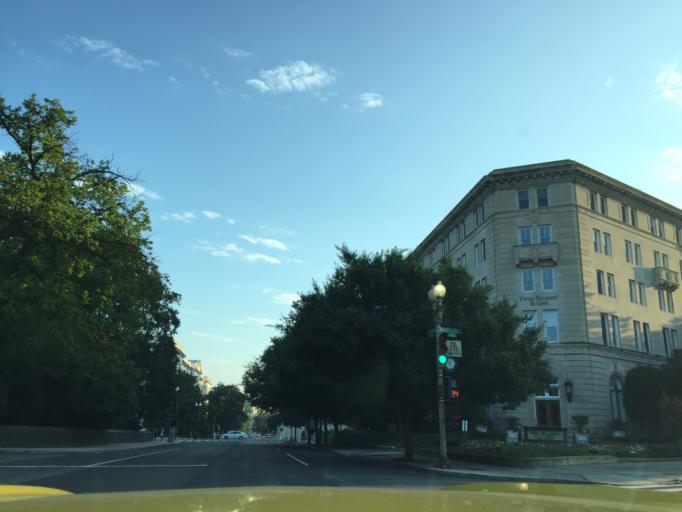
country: US
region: Washington, D.C.
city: Washington, D.C.
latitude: 38.8909
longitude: -77.0059
